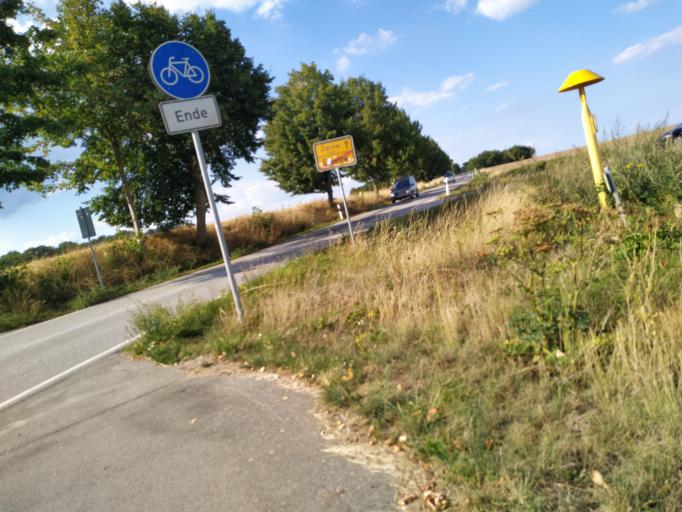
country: DE
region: Mecklenburg-Vorpommern
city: Gramkow
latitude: 53.9046
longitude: 11.3776
